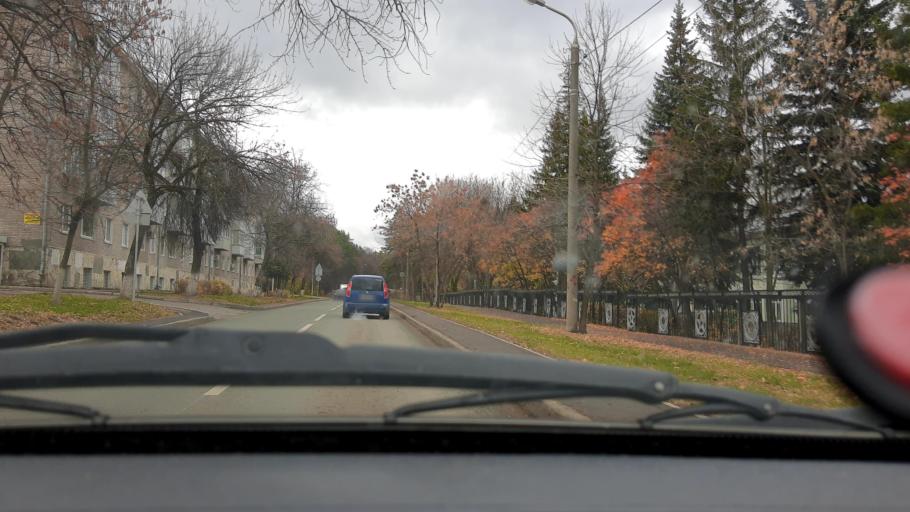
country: RU
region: Bashkortostan
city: Ufa
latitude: 54.7875
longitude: 56.0295
